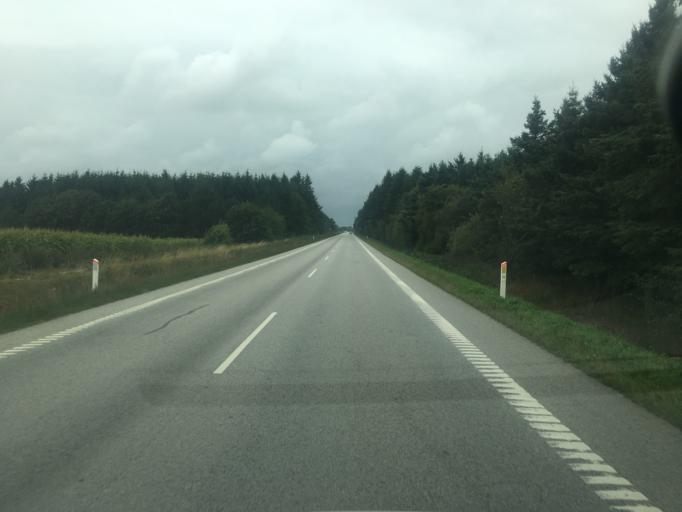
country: DK
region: South Denmark
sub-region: Haderslev Kommune
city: Vojens
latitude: 55.2232
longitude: 9.3006
